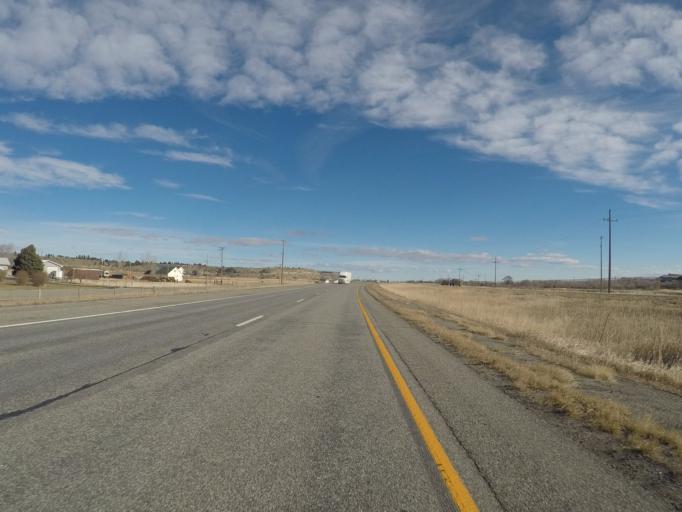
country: US
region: Montana
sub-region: Yellowstone County
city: Laurel
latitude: 45.6192
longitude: -108.9882
